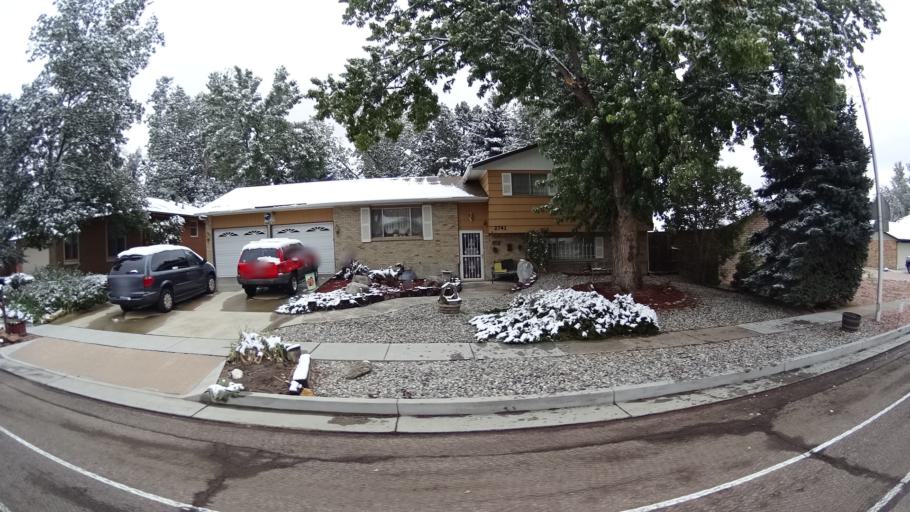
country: US
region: Colorado
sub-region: El Paso County
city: Colorado Springs
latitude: 38.8933
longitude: -104.7724
